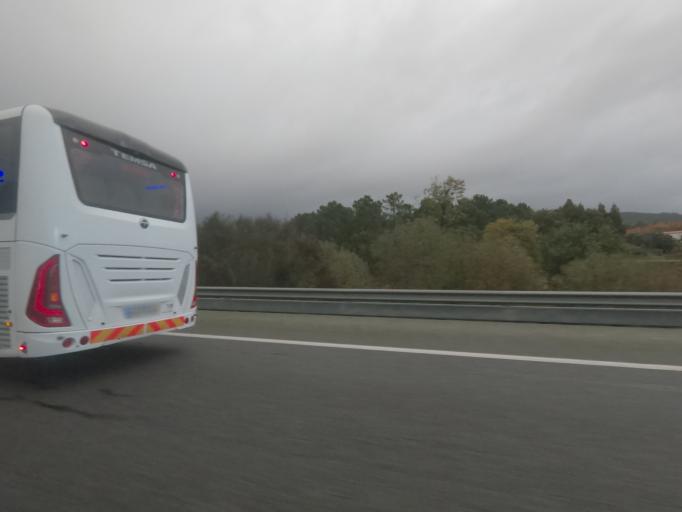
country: PT
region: Viana do Castelo
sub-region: Ponte de Lima
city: Ponte de Lima
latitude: 41.8033
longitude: -8.5852
